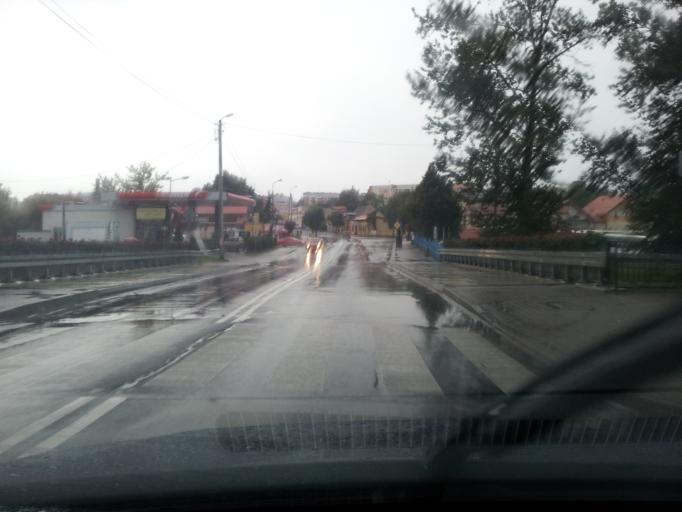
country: PL
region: Kujawsko-Pomorskie
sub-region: Powiat lipnowski
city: Lipno
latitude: 52.8466
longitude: 19.1796
